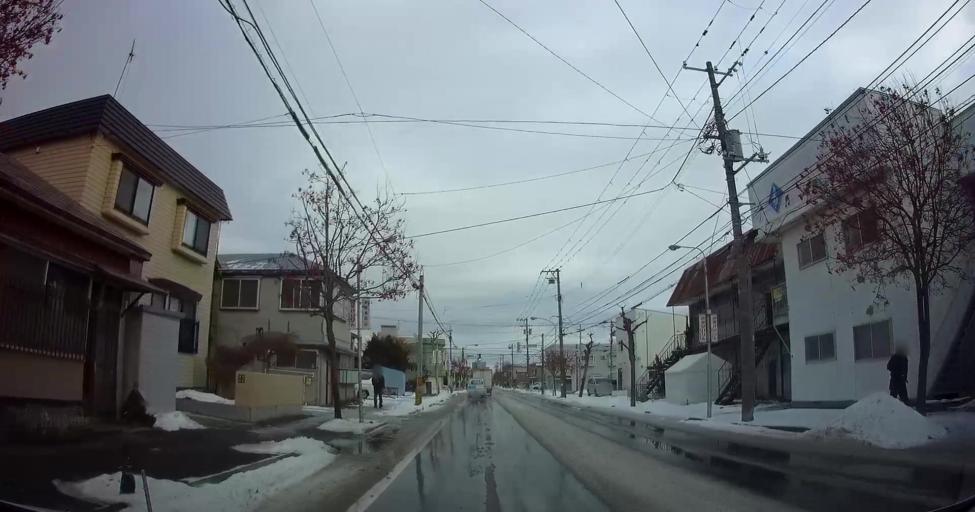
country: JP
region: Hokkaido
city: Hakodate
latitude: 41.7780
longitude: 140.7468
